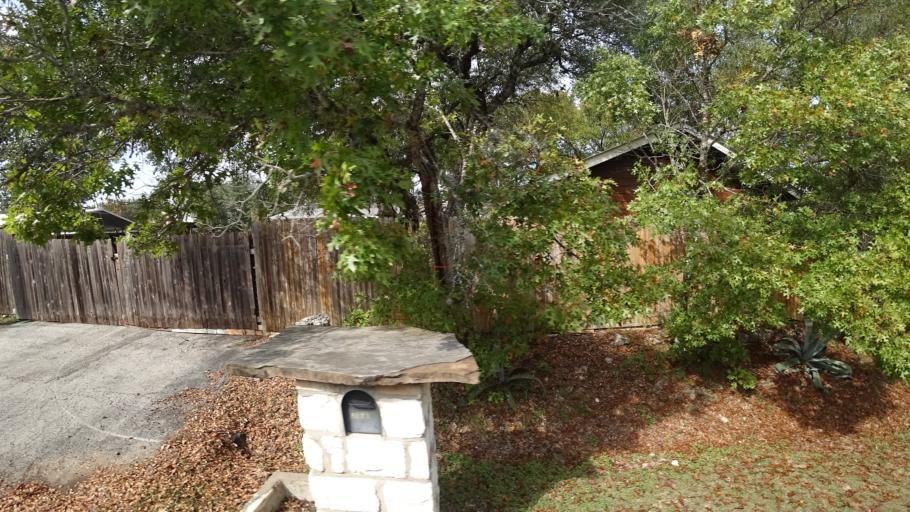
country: US
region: Texas
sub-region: Travis County
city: Hudson Bend
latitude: 30.3797
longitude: -97.9269
